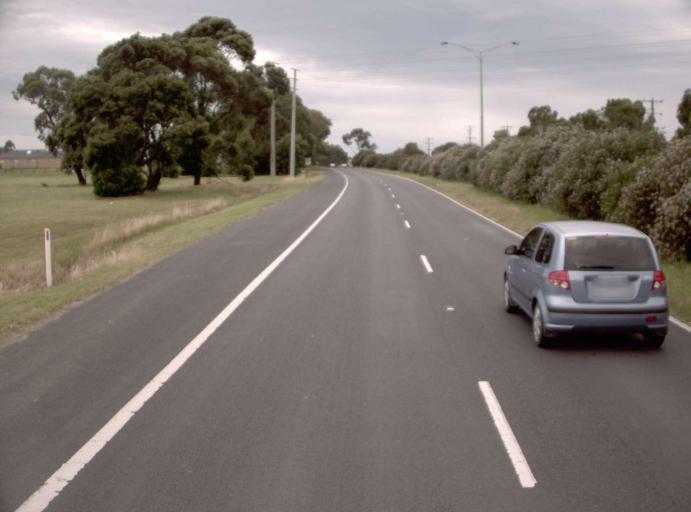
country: AU
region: Victoria
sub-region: Casey
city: Cranbourne North
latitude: -38.0890
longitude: 145.2795
